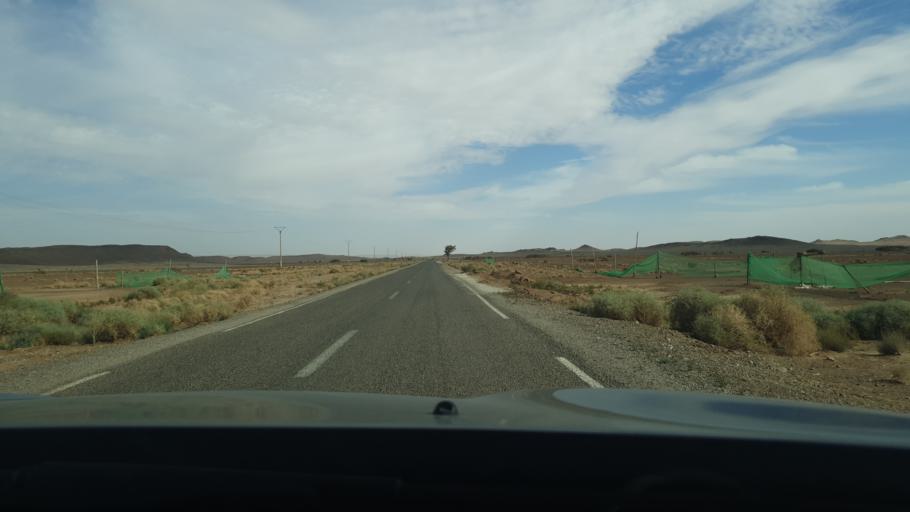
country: MA
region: Meknes-Tafilalet
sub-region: Errachidia
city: Goulmima
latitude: 31.5720
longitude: -4.8049
